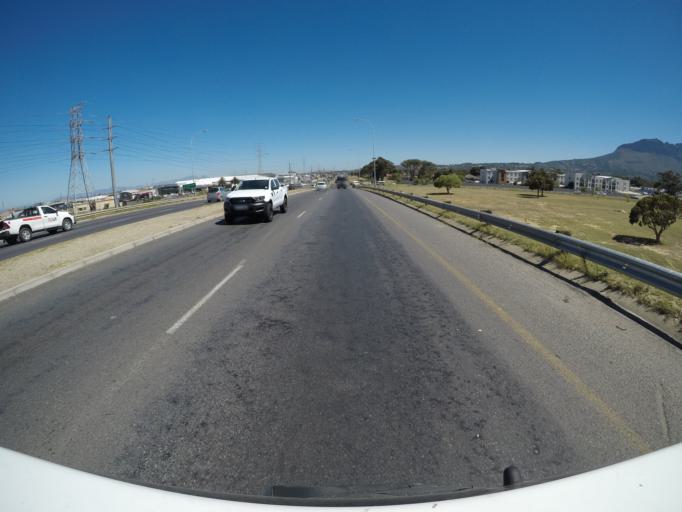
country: ZA
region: Western Cape
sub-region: Cape Winelands District Municipality
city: Stellenbosch
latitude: -34.0999
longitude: 18.8507
